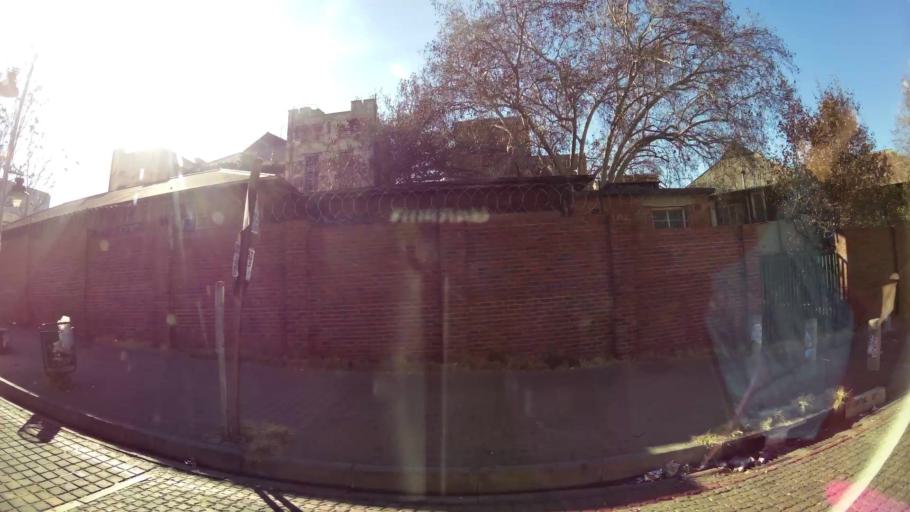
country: ZA
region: Gauteng
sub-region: City of Johannesburg Metropolitan Municipality
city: Johannesburg
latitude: -26.1925
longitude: 28.0438
